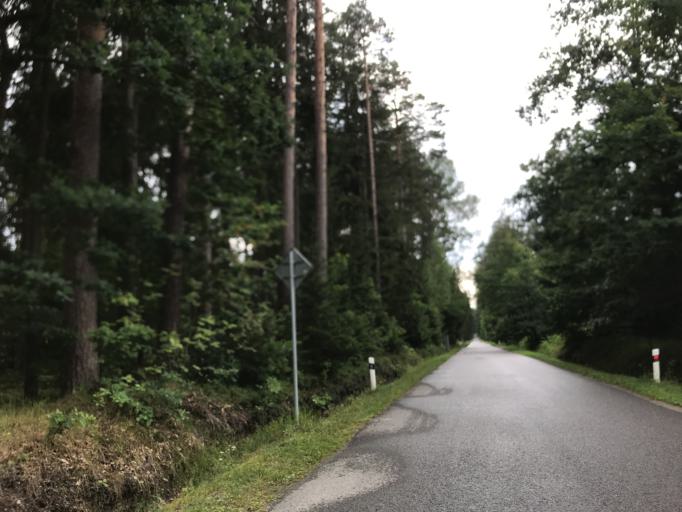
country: CZ
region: Jihocesky
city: Suchdol nad Luznici
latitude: 48.9466
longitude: 14.8700
